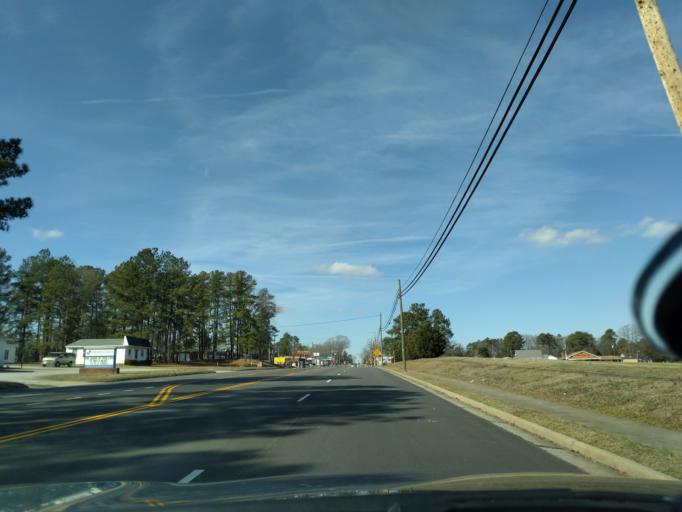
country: US
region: Virginia
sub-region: Nottoway County
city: Crewe
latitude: 37.1650
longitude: -78.1144
